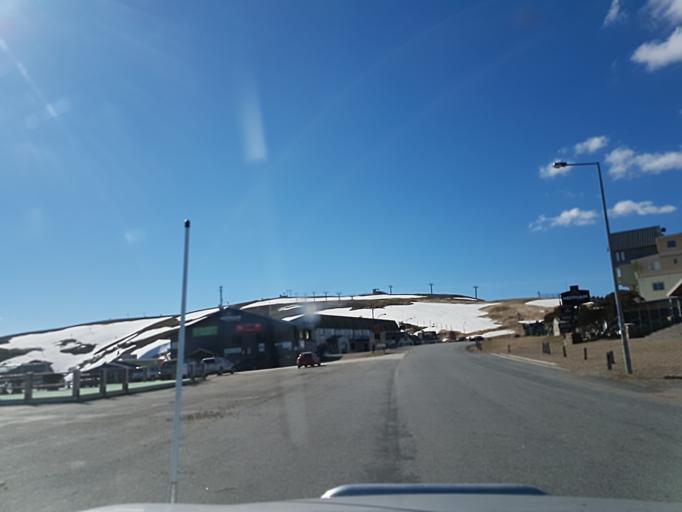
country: AU
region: Victoria
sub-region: Alpine
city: Mount Beauty
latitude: -36.9828
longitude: 147.1427
